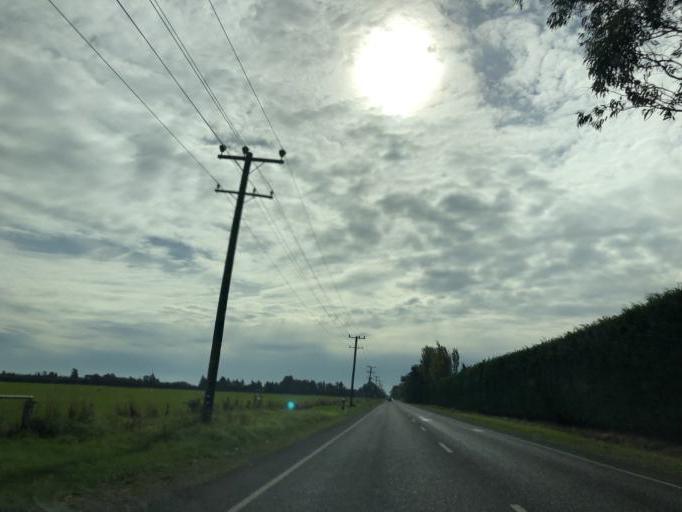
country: NZ
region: Canterbury
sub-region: Selwyn District
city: Lincoln
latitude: -43.6294
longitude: 172.4275
